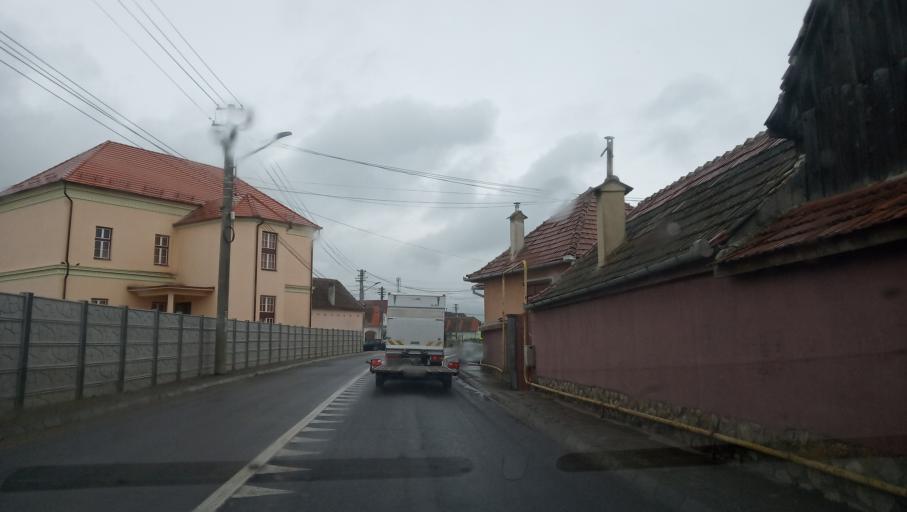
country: RO
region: Sibiu
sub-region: Comuna Cristian
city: Cristian
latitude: 45.7872
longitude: 24.0228
